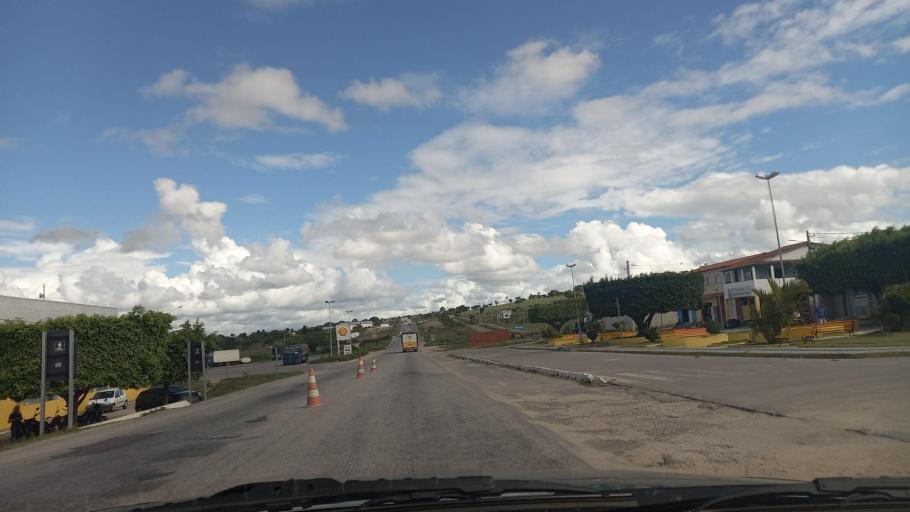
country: BR
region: Pernambuco
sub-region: Sao Joao
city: Sao Joao
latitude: -8.7551
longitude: -36.4308
